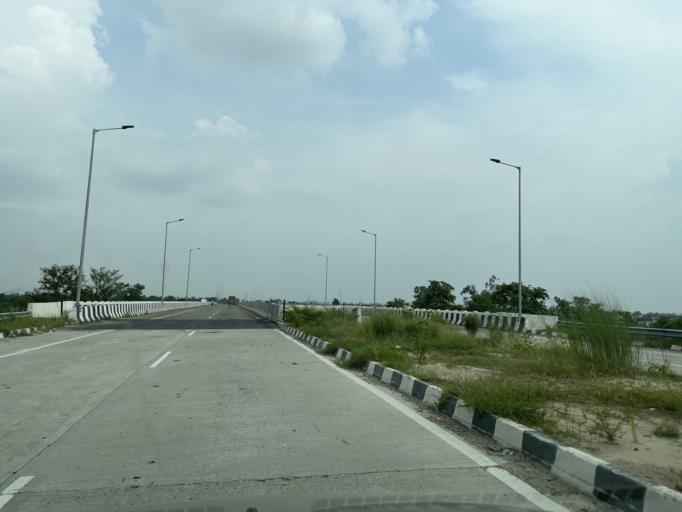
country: IN
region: Uttarakhand
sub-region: Udham Singh Nagar
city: Kashipur
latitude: 29.1743
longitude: 78.9451
